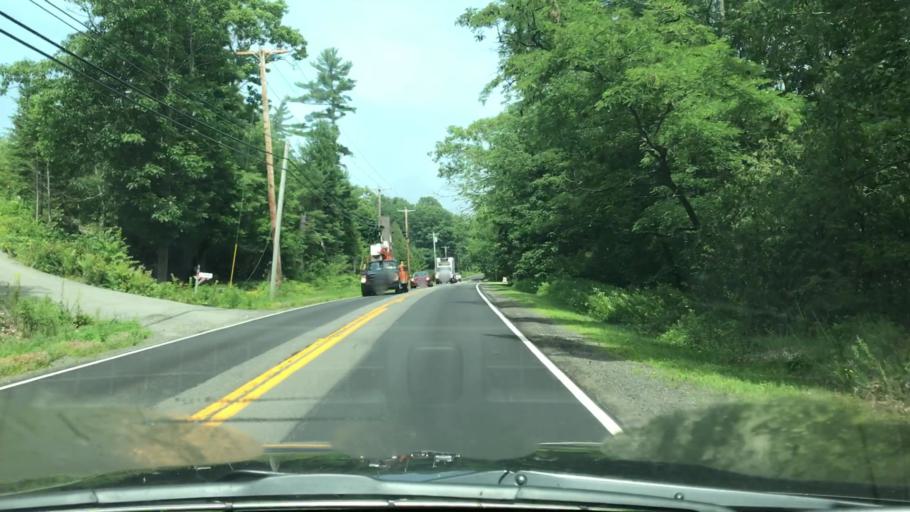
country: US
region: Maine
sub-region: Waldo County
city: Lincolnville
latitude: 44.2537
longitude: -69.0297
